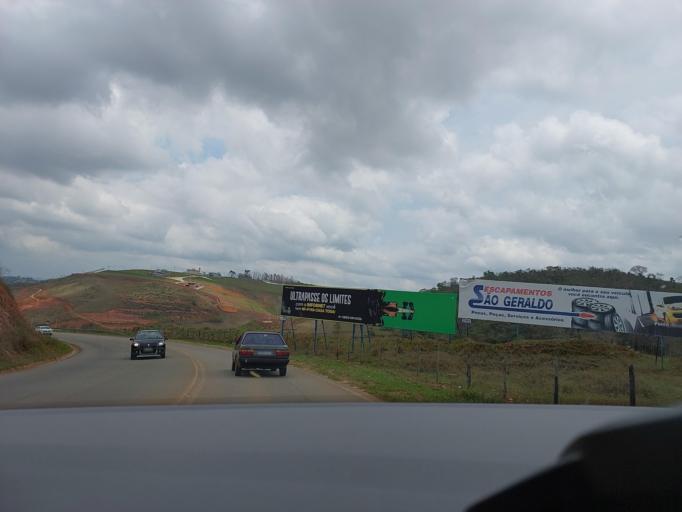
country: BR
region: Minas Gerais
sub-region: Ponte Nova
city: Ponte Nova
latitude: -20.3946
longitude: -42.8754
